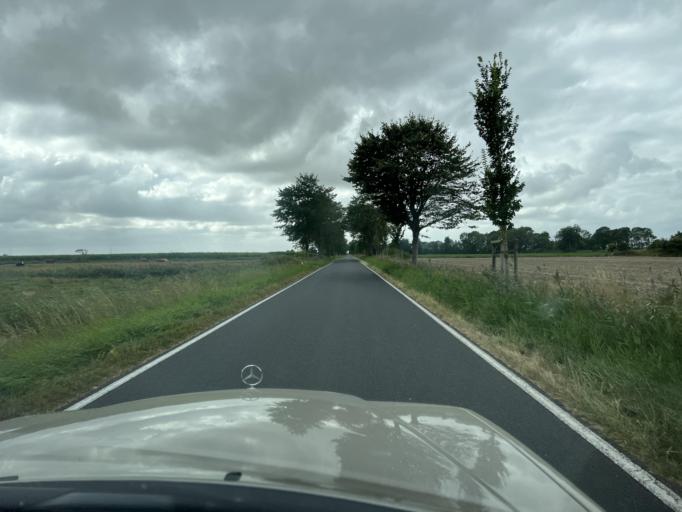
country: DE
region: Schleswig-Holstein
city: Lehe
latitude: 54.3325
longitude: 9.0121
